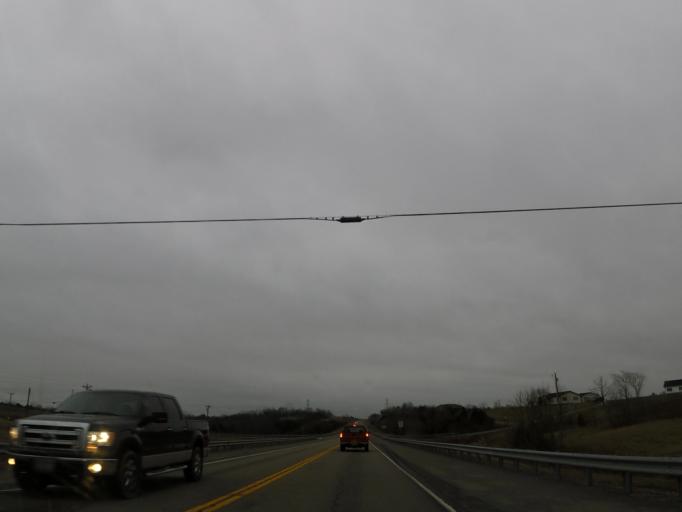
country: US
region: Kentucky
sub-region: Lincoln County
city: Stanford
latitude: 37.5177
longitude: -84.6105
